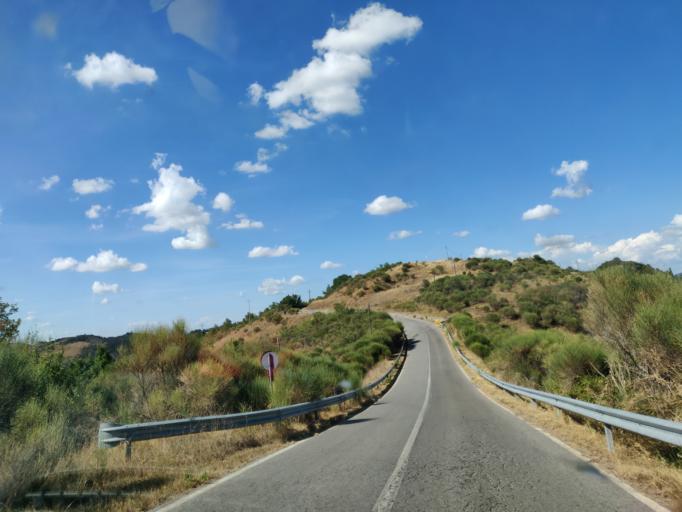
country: IT
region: Tuscany
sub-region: Provincia di Siena
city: Radicofani
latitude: 42.9386
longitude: 11.7336
